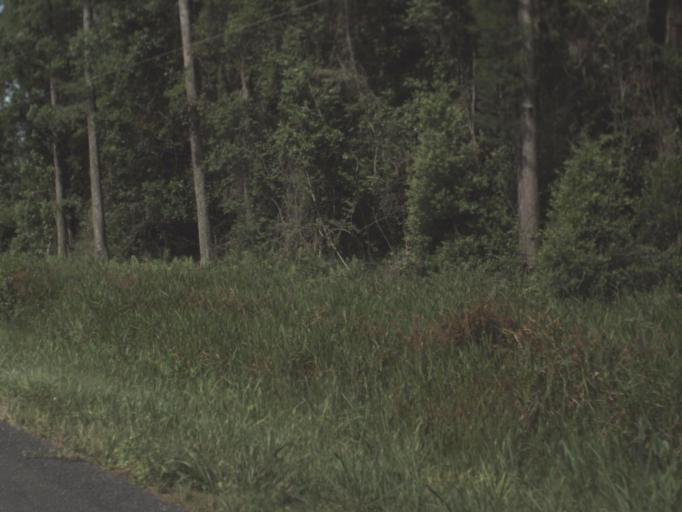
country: US
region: Florida
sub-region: Lafayette County
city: Mayo
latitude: 30.0075
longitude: -83.1927
